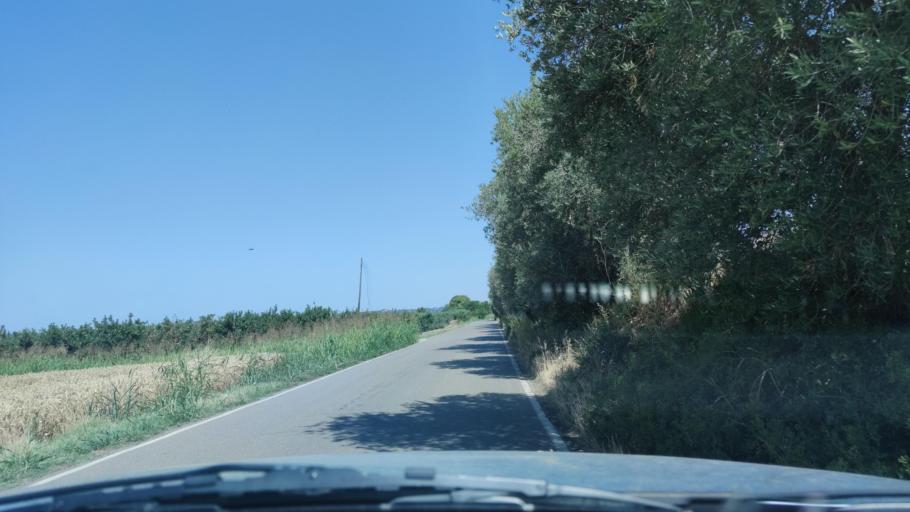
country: ES
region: Catalonia
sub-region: Provincia de Lleida
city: Torrefarrera
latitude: 41.6452
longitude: 0.5856
